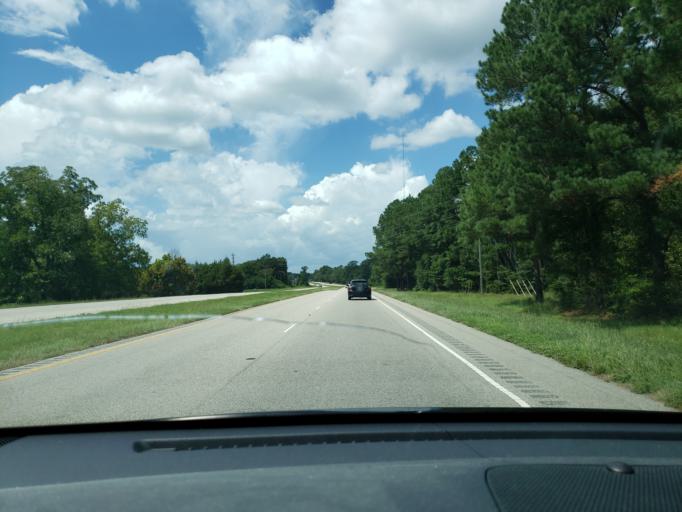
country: US
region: North Carolina
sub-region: Bladen County
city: Bladenboro
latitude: 34.7275
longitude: -78.7735
